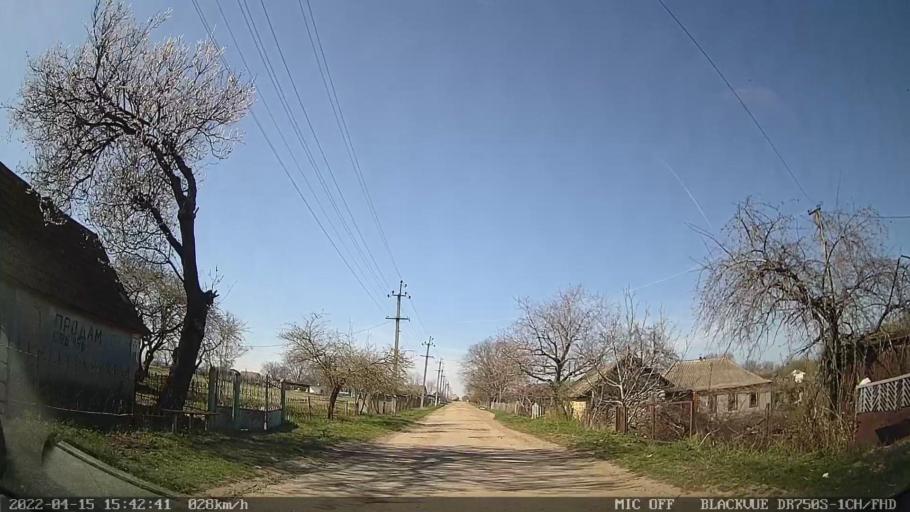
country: MD
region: Raionul Ocnita
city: Otaci
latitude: 48.3624
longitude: 27.9283
